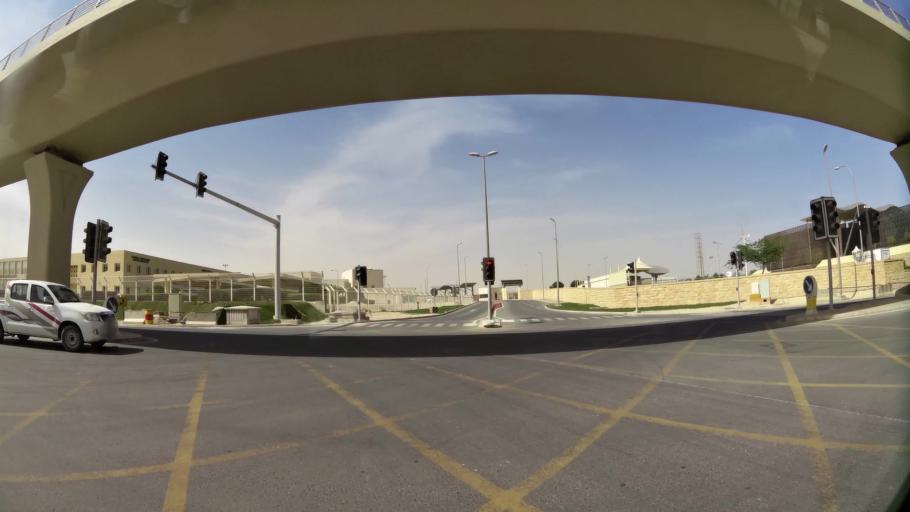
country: QA
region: Baladiyat ar Rayyan
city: Ar Rayyan
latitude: 25.3235
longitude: 51.4344
